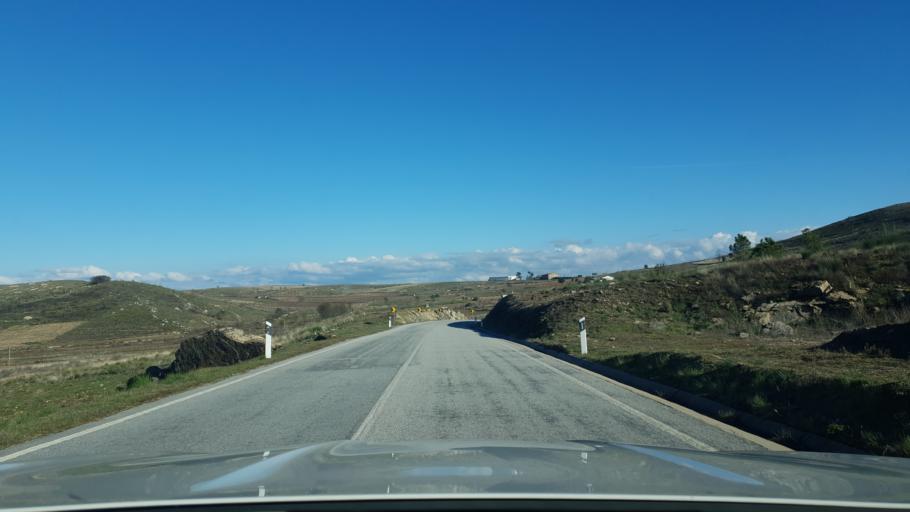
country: PT
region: Braganca
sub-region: Freixo de Espada A Cinta
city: Freixo de Espada a Cinta
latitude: 41.1812
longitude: -6.8044
